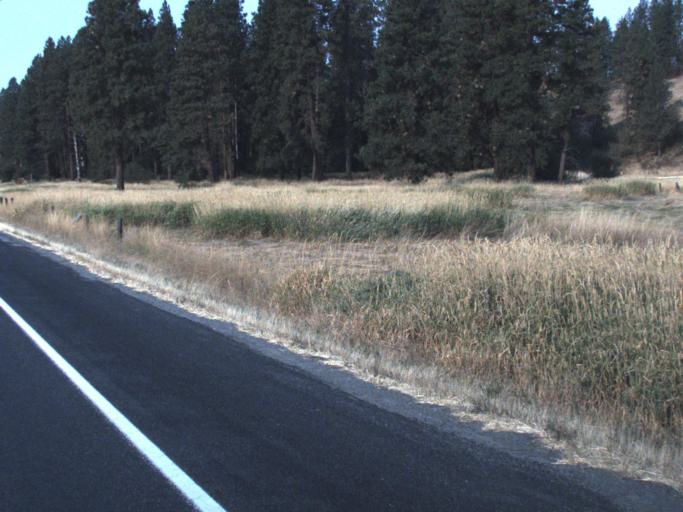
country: US
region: Idaho
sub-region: Benewah County
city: Plummer
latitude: 47.4415
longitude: -117.0809
